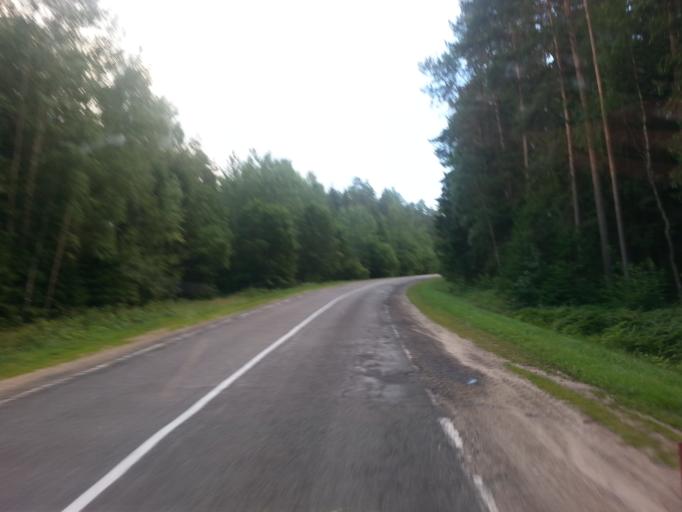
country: BY
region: Minsk
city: Il'ya
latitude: 54.5320
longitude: 27.2118
